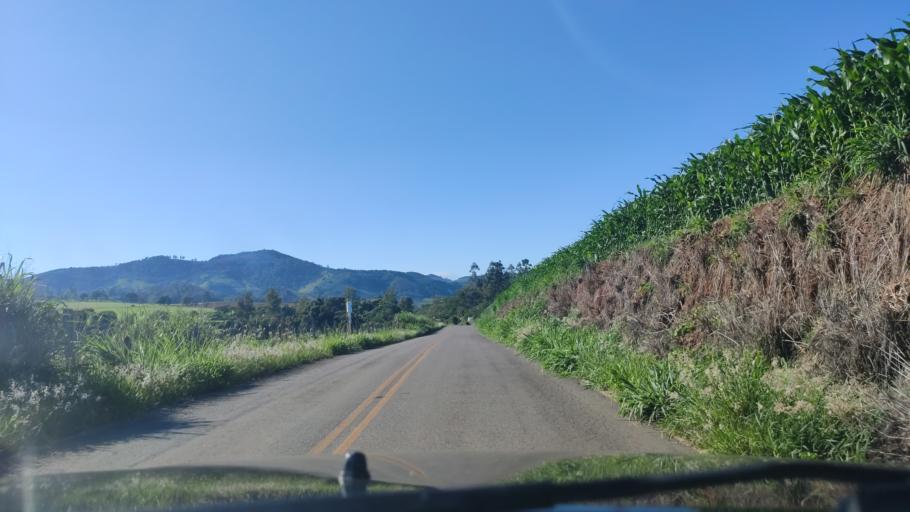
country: BR
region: Sao Paulo
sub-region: Serra Negra
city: Serra Negra
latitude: -22.5710
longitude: -46.6215
